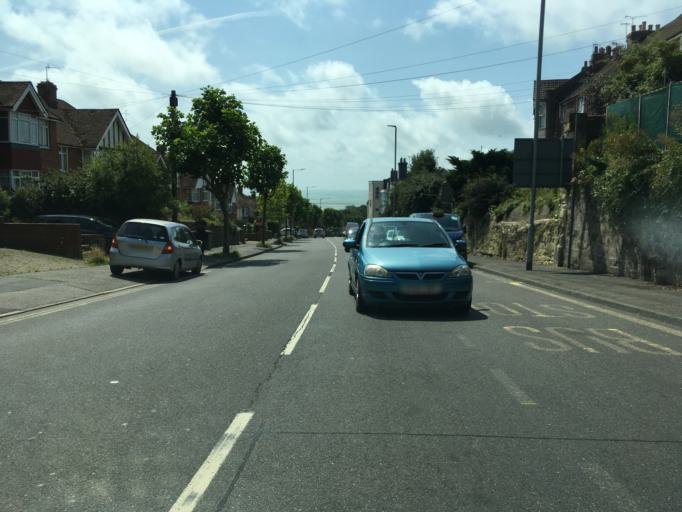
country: GB
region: England
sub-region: East Sussex
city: Hastings
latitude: 50.8682
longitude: 0.6006
